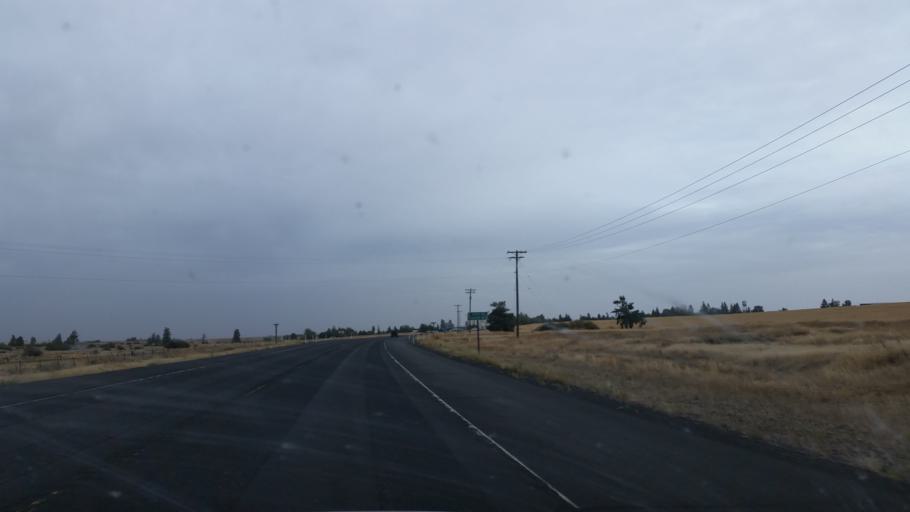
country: US
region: Washington
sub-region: Spokane County
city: Medical Lake
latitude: 47.6683
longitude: -117.9027
